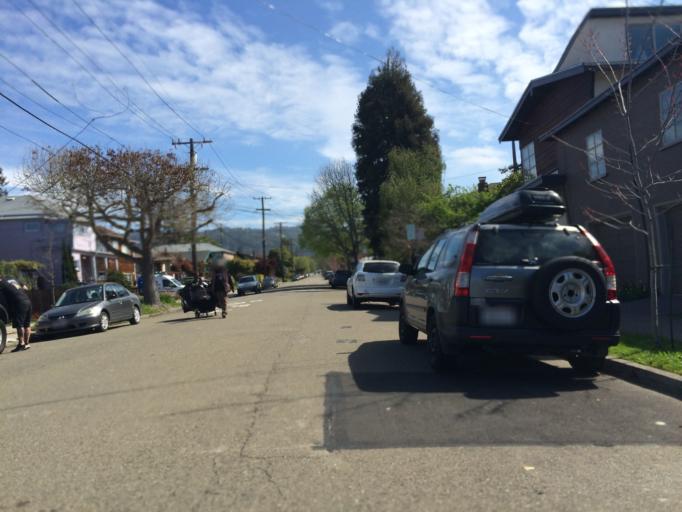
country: US
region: California
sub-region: Alameda County
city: Berkeley
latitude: 37.8750
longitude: -122.2817
